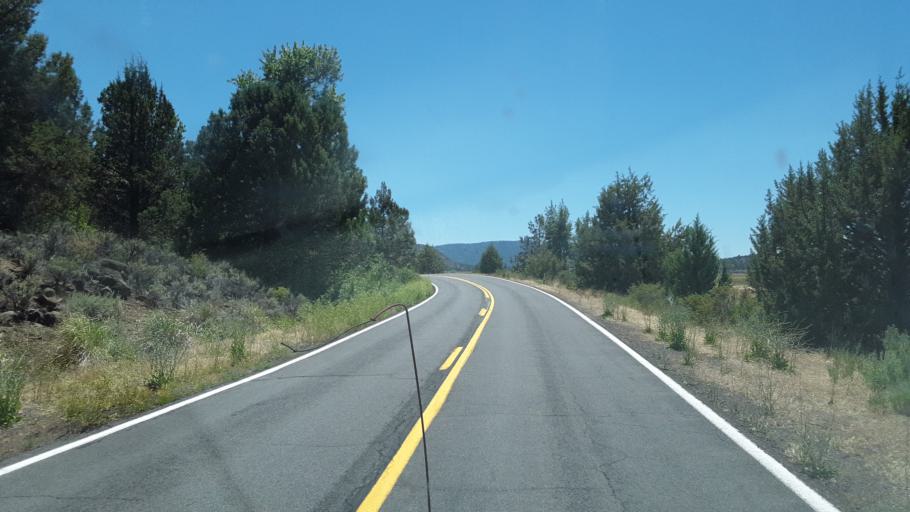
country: US
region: California
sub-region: Lassen County
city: Susanville
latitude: 40.6667
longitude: -120.6572
